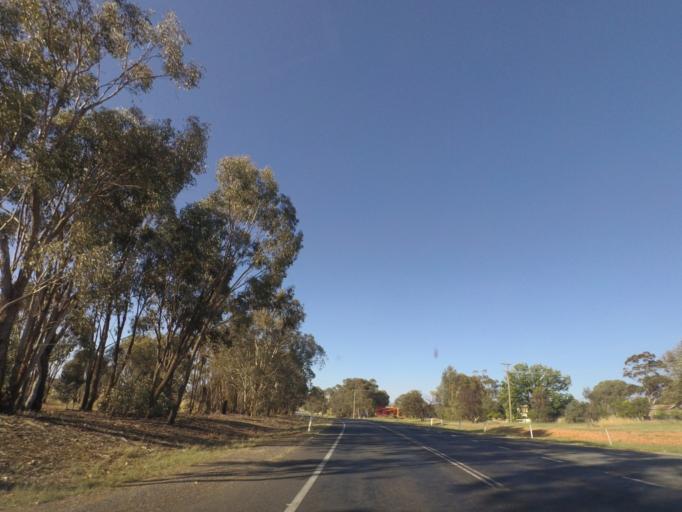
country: AU
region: New South Wales
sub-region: Wagga Wagga
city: Forest Hill
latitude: -35.2713
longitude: 147.7440
